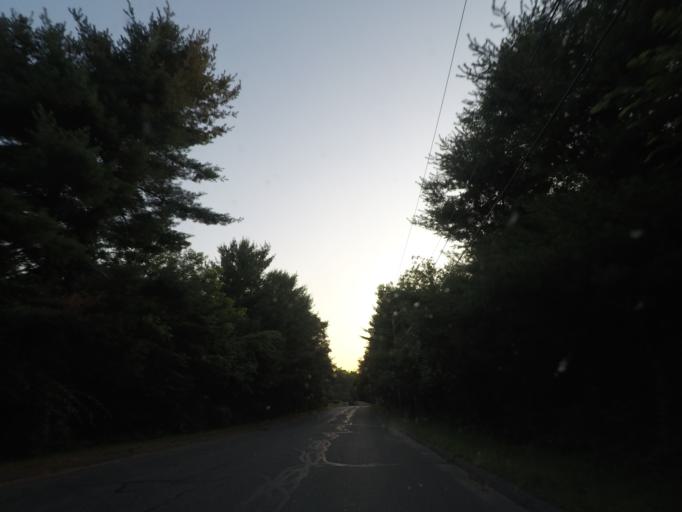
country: US
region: Massachusetts
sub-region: Hampden County
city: Palmer
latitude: 42.1680
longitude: -72.3284
